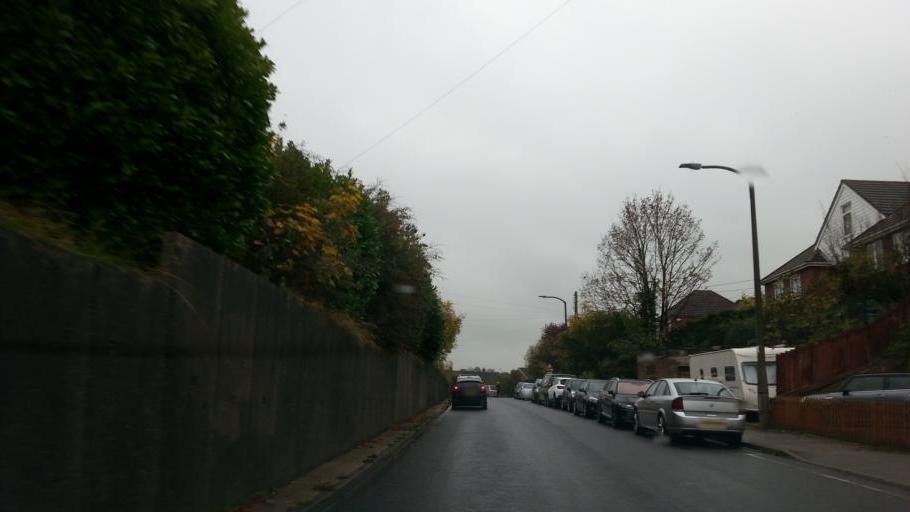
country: GB
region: England
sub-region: Suffolk
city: Haverhill
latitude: 52.0840
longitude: 0.4317
